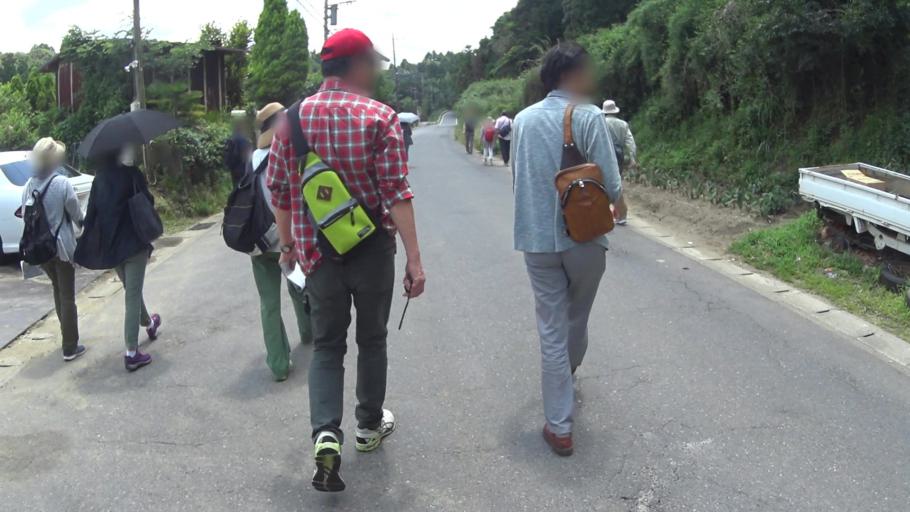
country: JP
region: Chiba
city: Sawara
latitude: 35.8909
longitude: 140.5271
